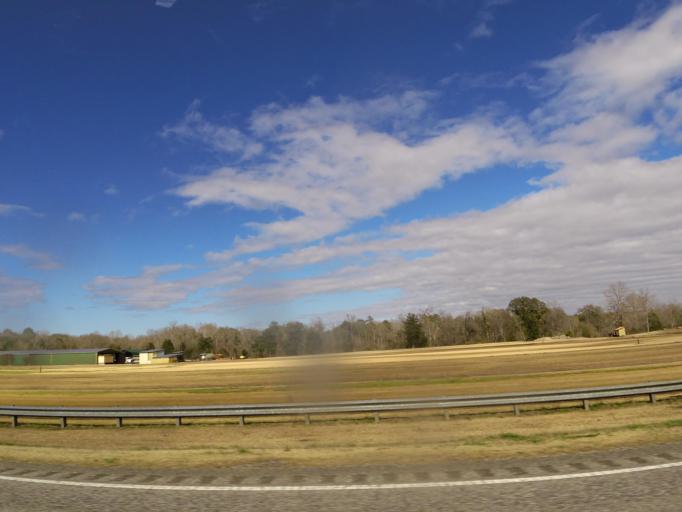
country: US
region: Alabama
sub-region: Barbour County
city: Clayton
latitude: 32.0133
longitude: -85.3048
